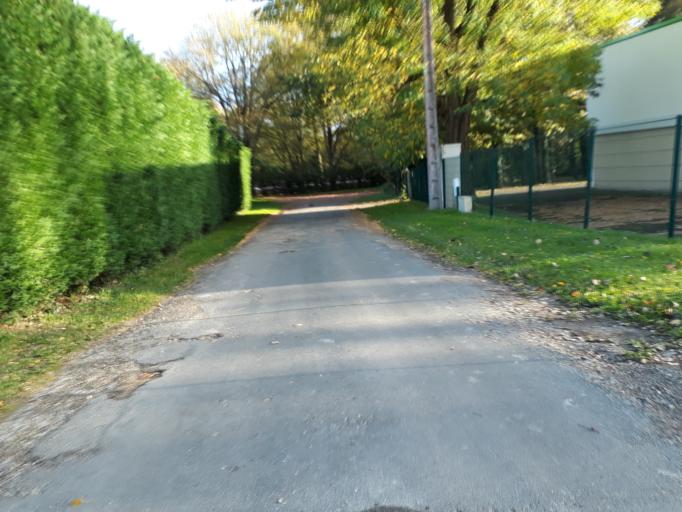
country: FR
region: Ile-de-France
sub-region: Departement de Seine-et-Marne
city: Bois-le-Roi
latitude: 48.4631
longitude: 2.7044
